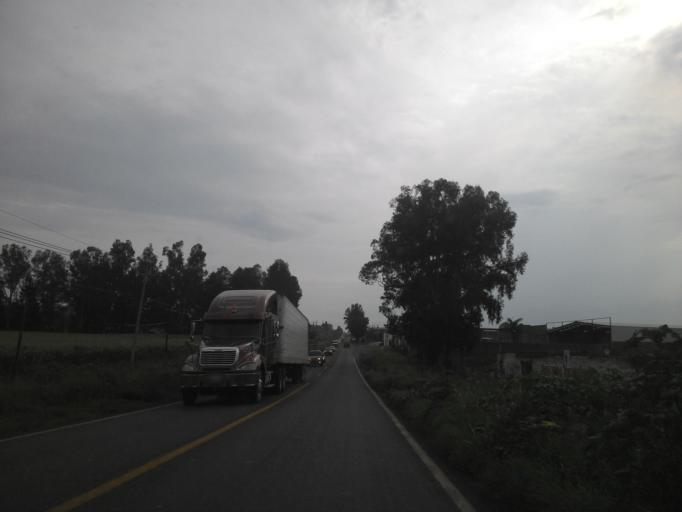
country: MX
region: Jalisco
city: Tepatitlan de Morelos
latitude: 20.7762
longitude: -102.7944
